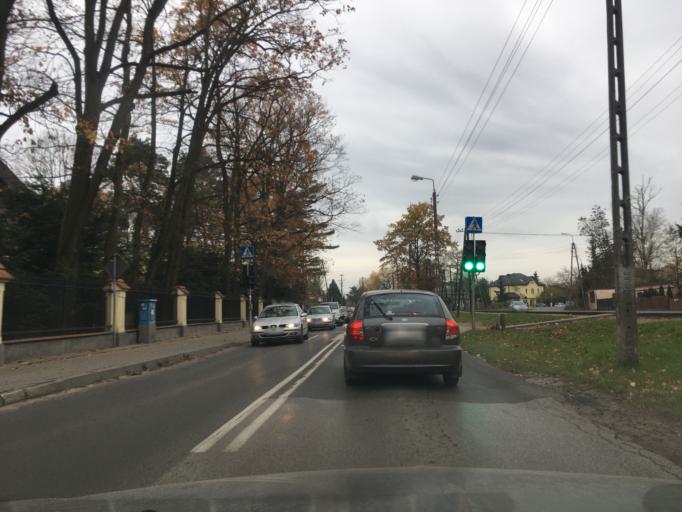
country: PL
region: Masovian Voivodeship
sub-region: Powiat piaseczynski
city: Piaseczno
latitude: 52.0575
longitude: 21.0085
